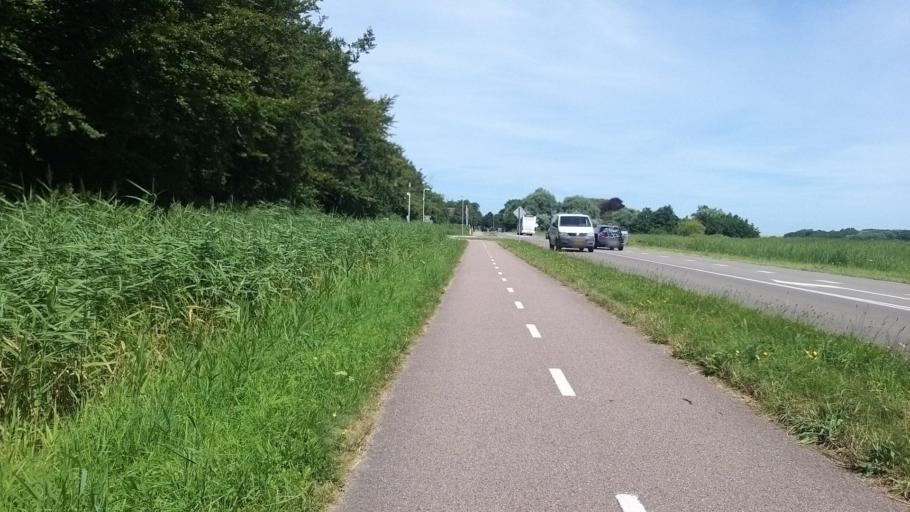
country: NL
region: North Holland
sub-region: Gemeente Texel
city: Den Burg
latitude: 53.1482
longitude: 4.8620
